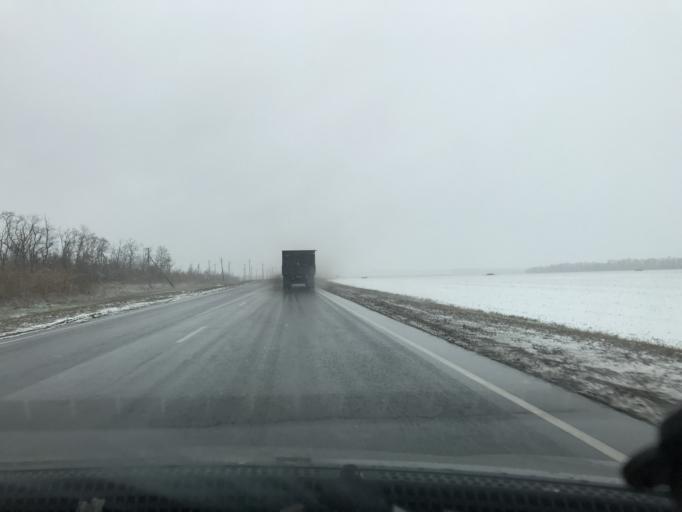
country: RU
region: Rostov
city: Yegorlykskaya
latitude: 46.5784
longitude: 40.6320
